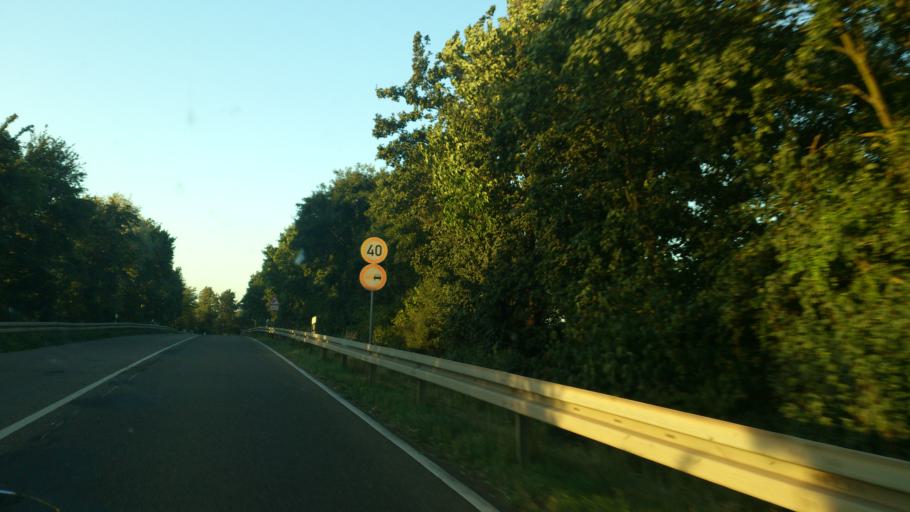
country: DE
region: Hesse
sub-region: Regierungsbezirk Darmstadt
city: Hattersheim
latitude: 50.0477
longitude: 8.4799
